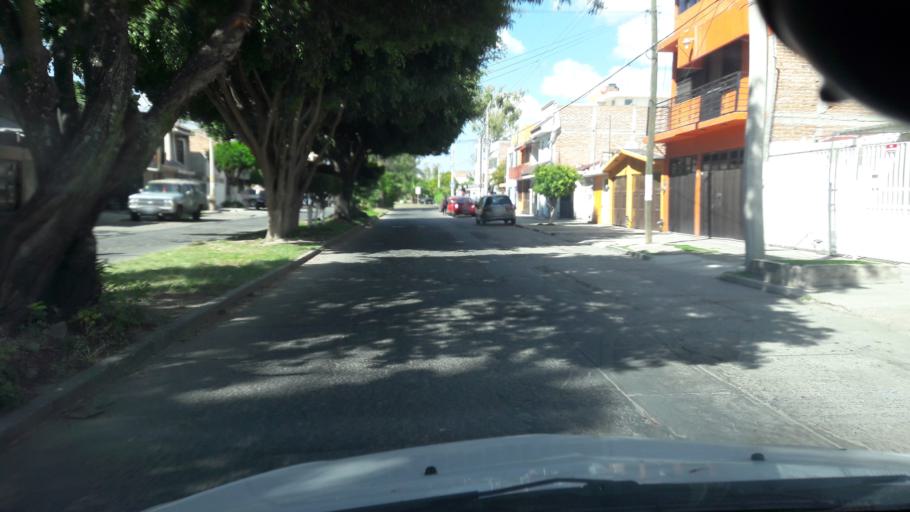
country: MX
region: Guanajuato
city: Leon
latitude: 21.1769
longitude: -101.6660
